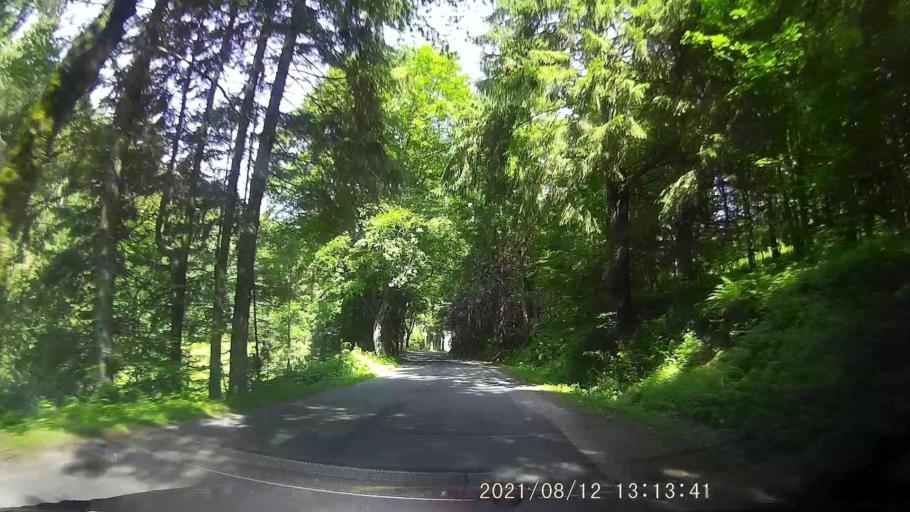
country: PL
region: Lower Silesian Voivodeship
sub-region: Powiat klodzki
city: Stronie Slaskie
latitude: 50.2551
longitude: 16.8547
